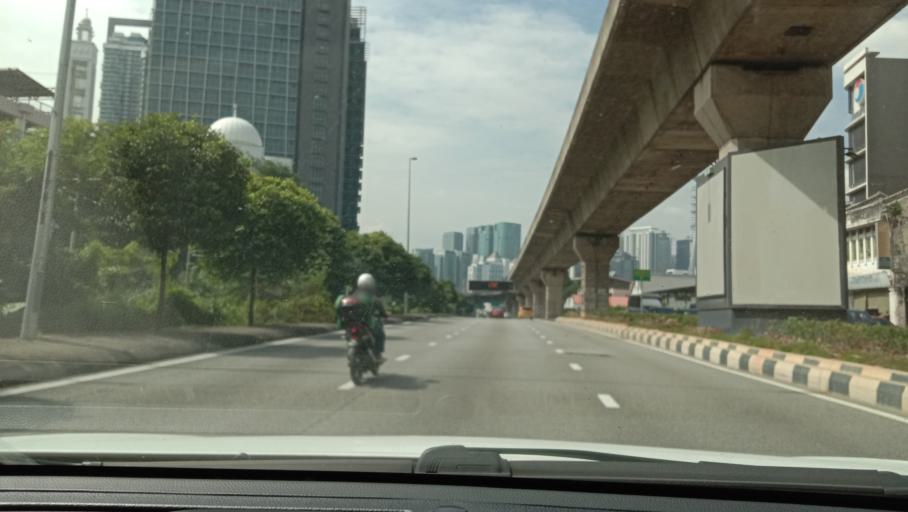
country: MY
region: Kuala Lumpur
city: Kuala Lumpur
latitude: 3.1220
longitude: 101.6753
